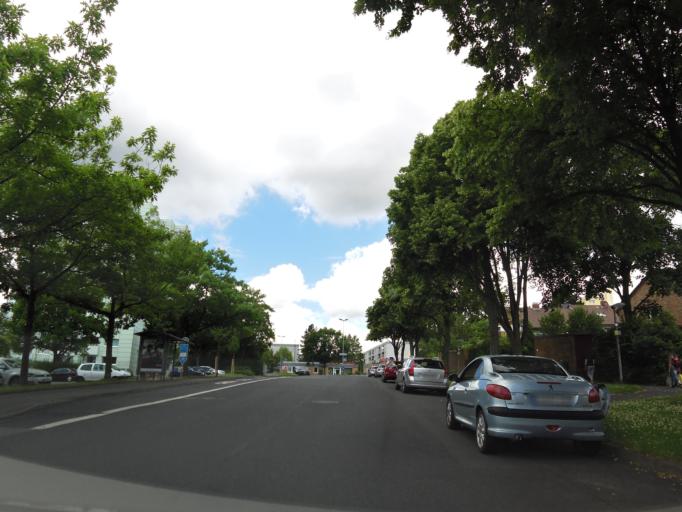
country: DE
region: Lower Saxony
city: Goettingen
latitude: 51.5158
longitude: 9.9713
